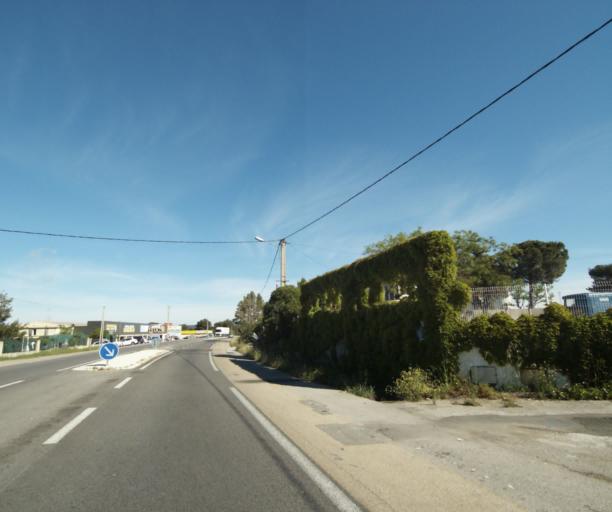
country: FR
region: Provence-Alpes-Cote d'Azur
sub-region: Departement des Bouches-du-Rhone
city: Rognac
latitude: 43.4737
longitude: 5.2288
